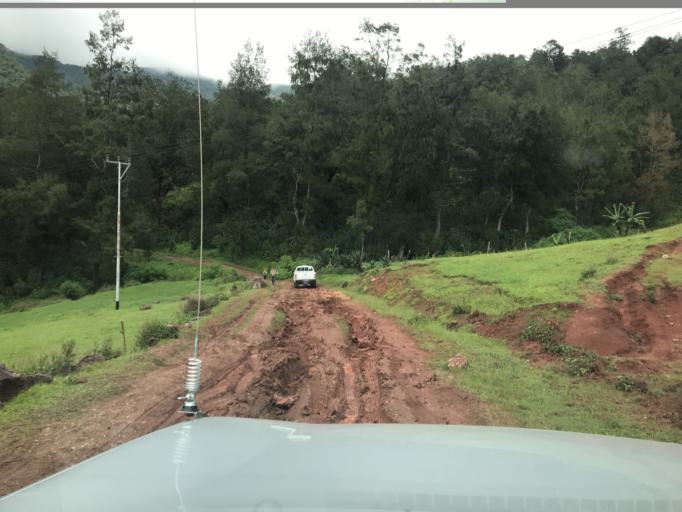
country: TL
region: Aileu
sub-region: Aileu Villa
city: Aileu
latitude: -8.8618
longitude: 125.5660
